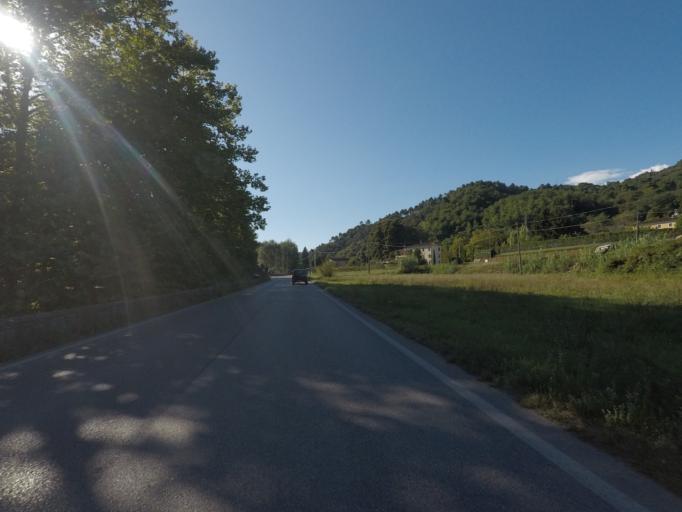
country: IT
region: Tuscany
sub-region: Provincia di Lucca
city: Massarosa
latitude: 43.9002
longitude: 10.3842
